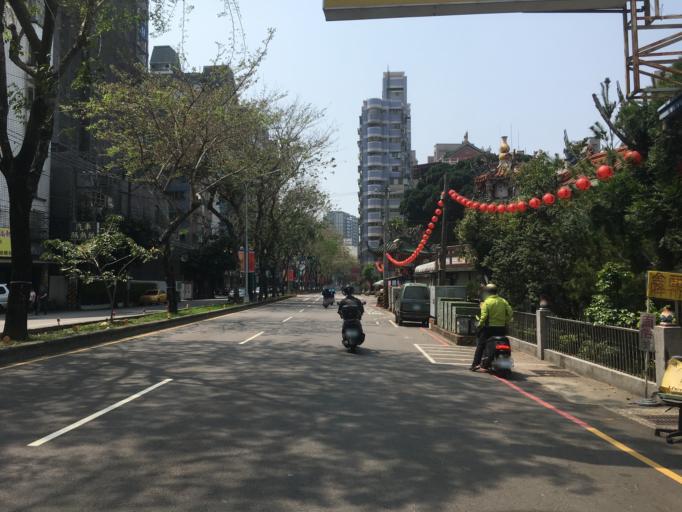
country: TW
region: Taiwan
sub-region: Taichung City
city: Taichung
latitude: 24.1830
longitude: 120.6930
